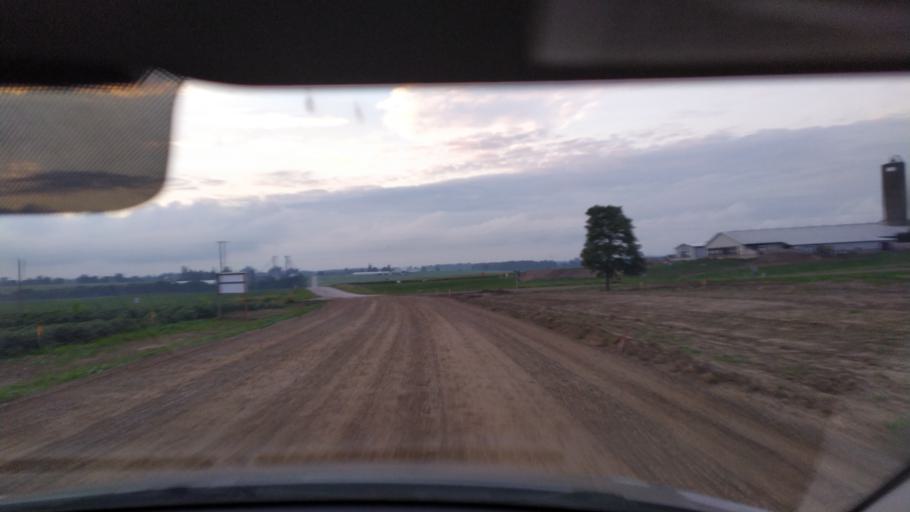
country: CA
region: Ontario
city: Kitchener
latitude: 43.3282
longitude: -80.6188
